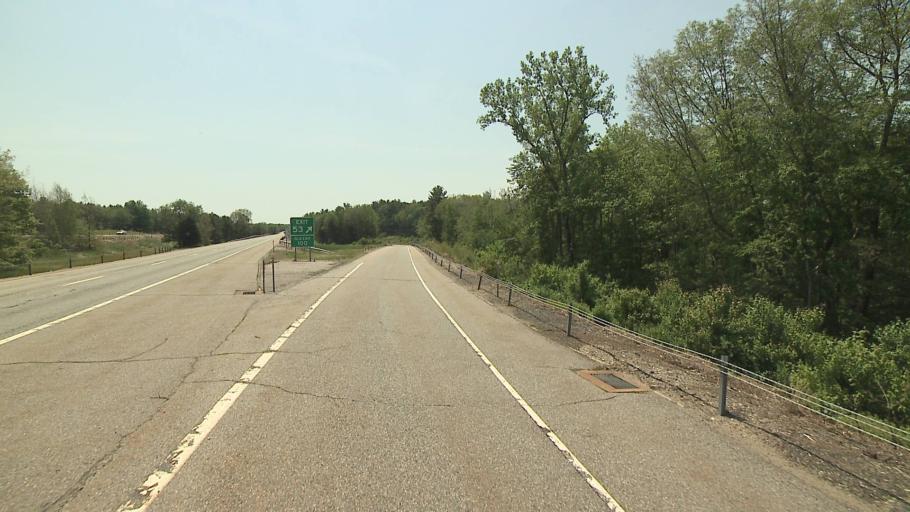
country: US
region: Massachusetts
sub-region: Worcester County
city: Webster
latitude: 42.0109
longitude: -71.8562
